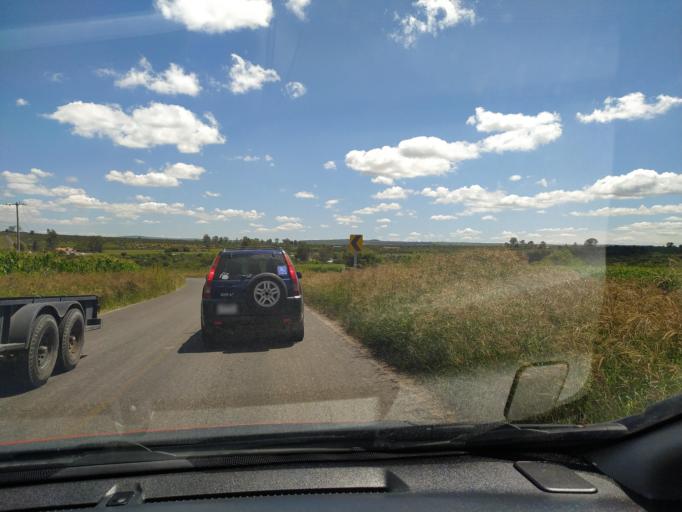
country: MX
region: Jalisco
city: San Julian
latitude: 21.0006
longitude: -102.0976
